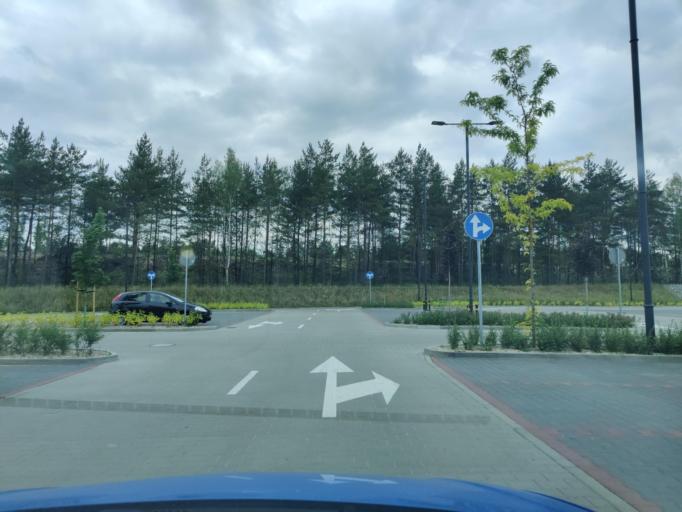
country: PL
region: Silesian Voivodeship
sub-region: Myslowice
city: Myslowice
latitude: 50.2294
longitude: 19.1743
